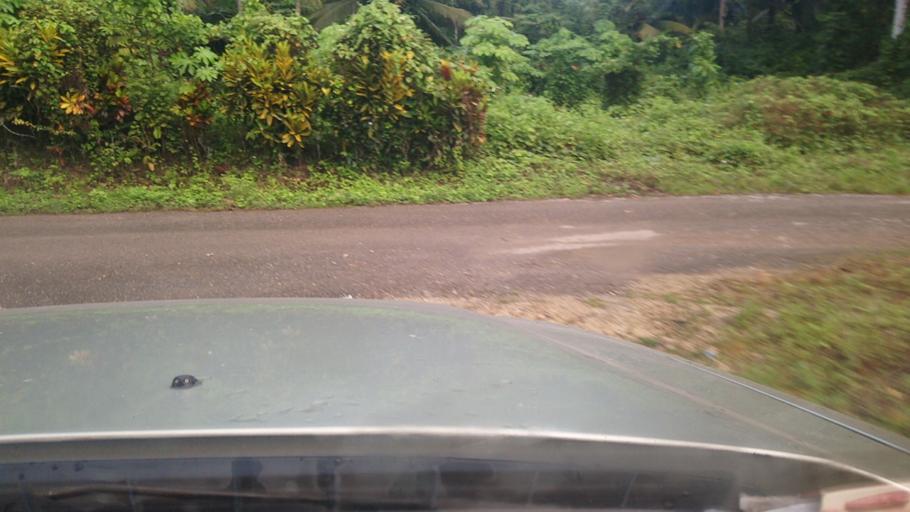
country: TT
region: Couva-Tabaquite-Talparo
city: Tabaquite
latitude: 10.4816
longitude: -61.2081
